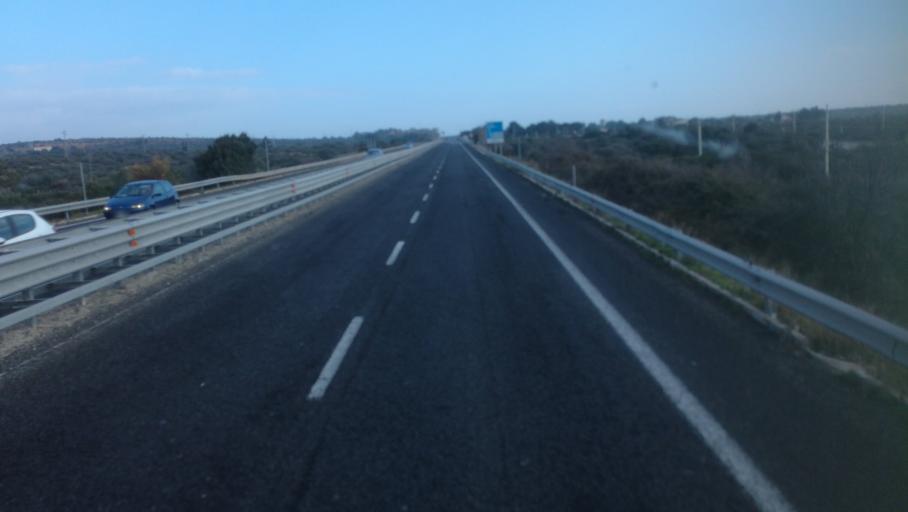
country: IT
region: Apulia
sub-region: Provincia di Taranto
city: Paolo VI
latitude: 40.5594
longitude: 17.2801
